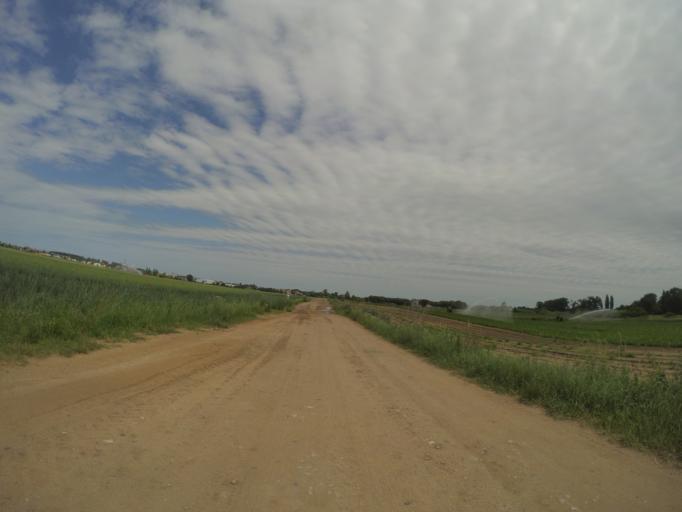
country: CZ
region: Central Bohemia
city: Lysa nad Labem
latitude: 50.1837
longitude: 14.8367
